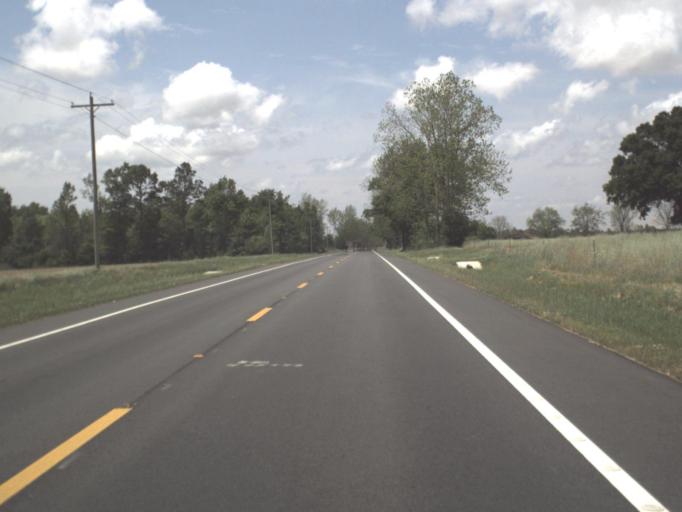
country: US
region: Florida
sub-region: Escambia County
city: Century
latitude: 30.8607
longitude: -87.1539
